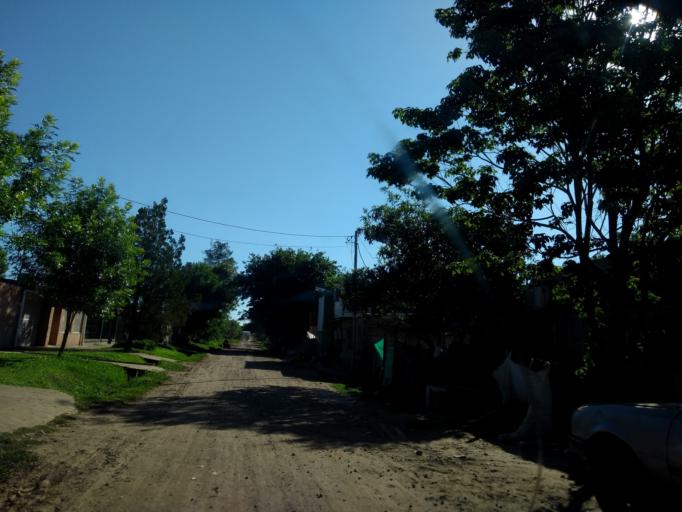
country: AR
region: Chaco
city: Fontana
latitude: -27.4114
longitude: -59.0414
